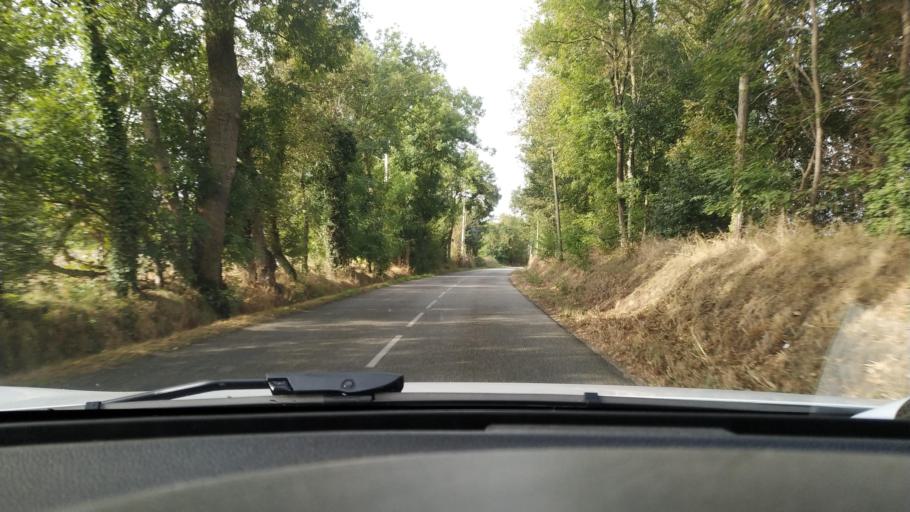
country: FR
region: Midi-Pyrenees
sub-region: Departement de la Haute-Garonne
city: Auterive
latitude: 43.3289
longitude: 1.4452
